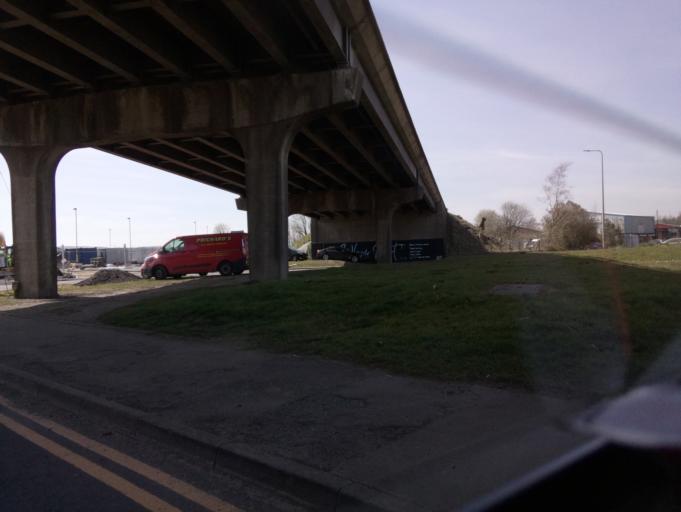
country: GB
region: Wales
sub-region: Merthyr Tydfil County Borough
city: Merthyr Tydfil
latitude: 51.7678
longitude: -3.3569
